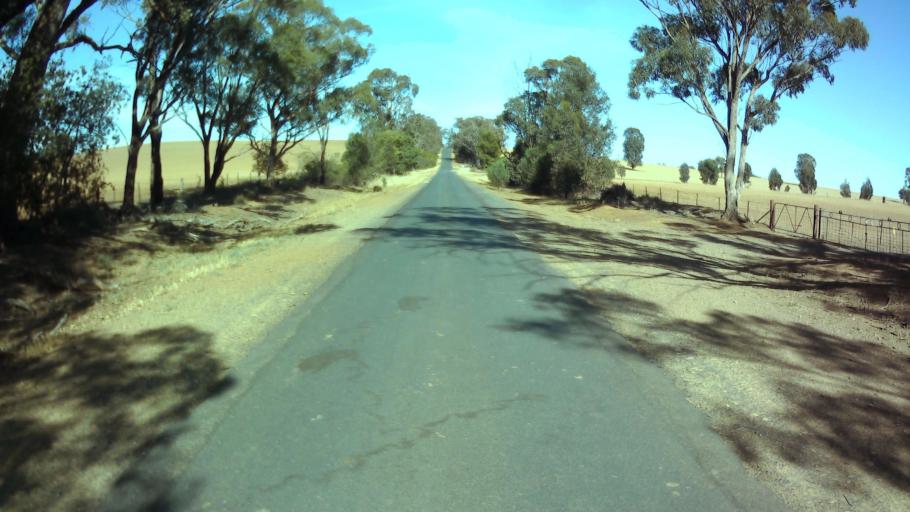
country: AU
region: New South Wales
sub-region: Weddin
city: Grenfell
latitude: -33.9065
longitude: 148.0700
